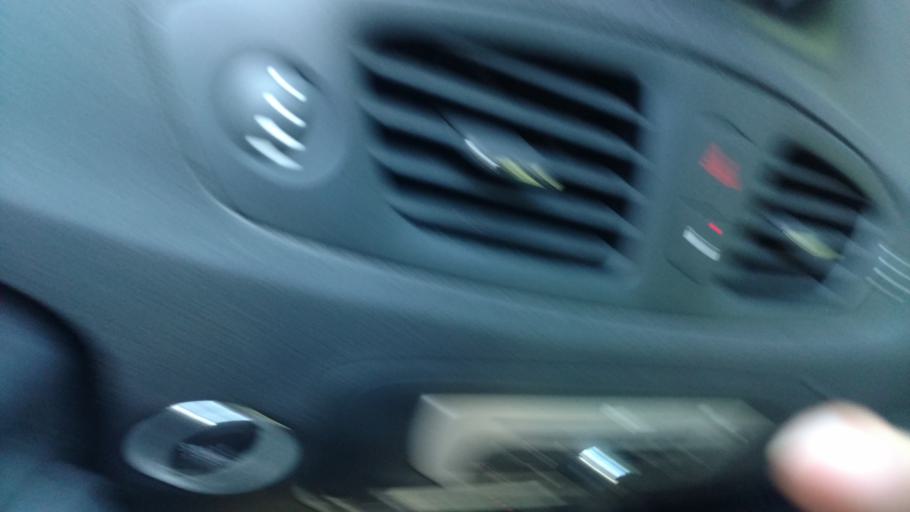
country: FR
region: Rhone-Alpes
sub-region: Departement de la Savoie
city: Villargondran
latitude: 45.2376
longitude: 6.4073
